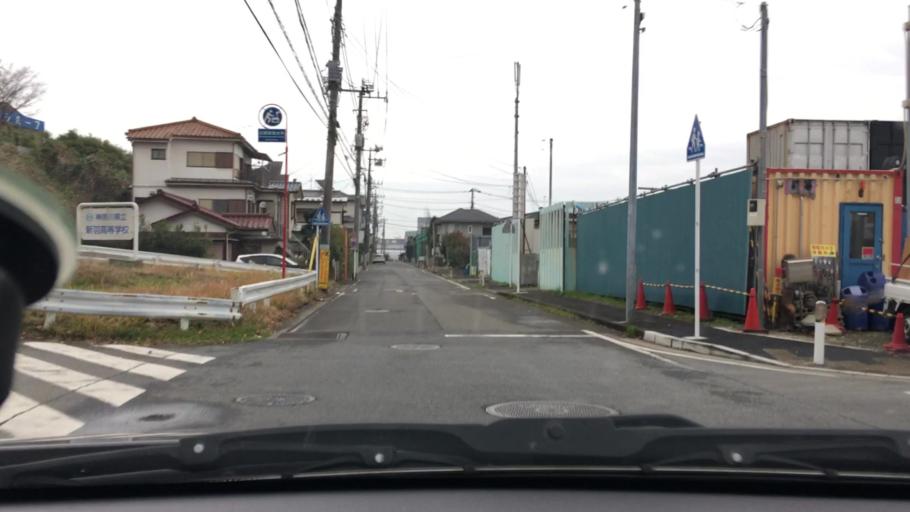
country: JP
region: Kanagawa
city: Yokohama
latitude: 35.5193
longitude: 139.6042
